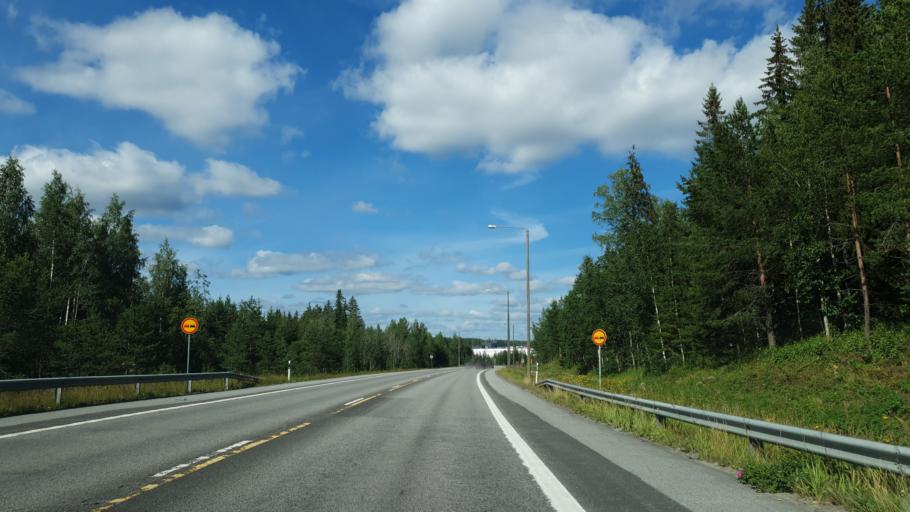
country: FI
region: Central Finland
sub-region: Jyvaeskylae
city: Muurame
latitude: 62.1766
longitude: 25.6799
